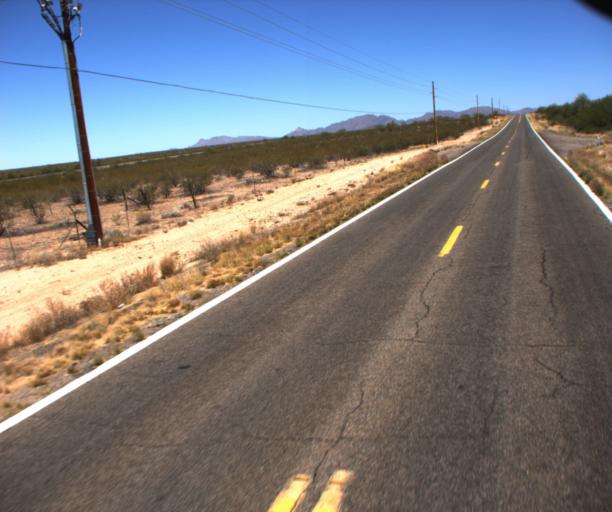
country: US
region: Arizona
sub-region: Yavapai County
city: Congress
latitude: 34.0577
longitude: -112.8177
